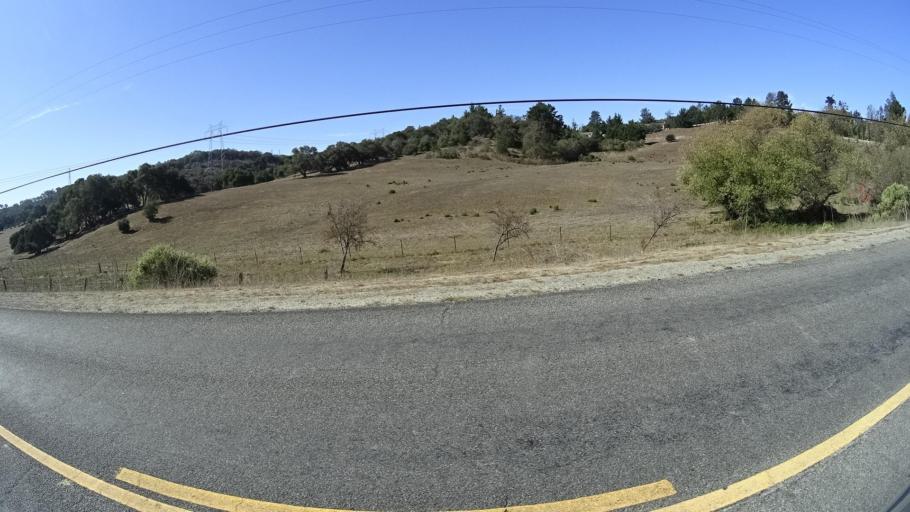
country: US
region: California
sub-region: Monterey County
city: Prunedale
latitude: 36.7840
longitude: -121.6105
